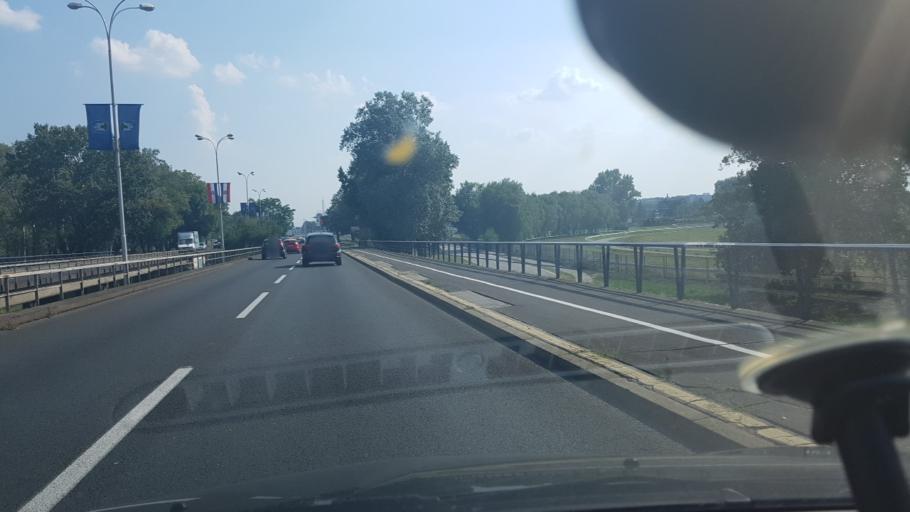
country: HR
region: Grad Zagreb
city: Novi Zagreb
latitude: 45.7866
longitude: 15.9797
